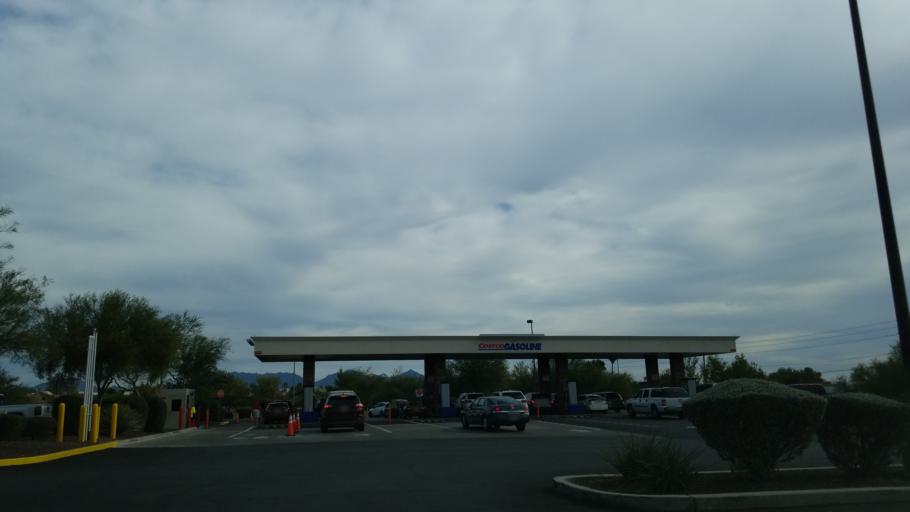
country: US
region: Arizona
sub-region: Maricopa County
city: Paradise Valley
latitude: 33.6701
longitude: -112.0275
